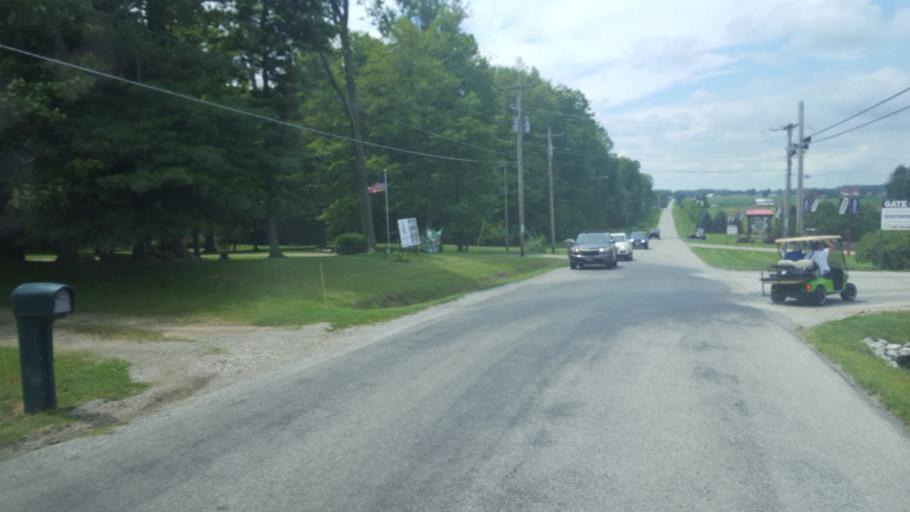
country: US
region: Ohio
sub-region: Richland County
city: Lexington
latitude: 40.6807
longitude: -82.6379
